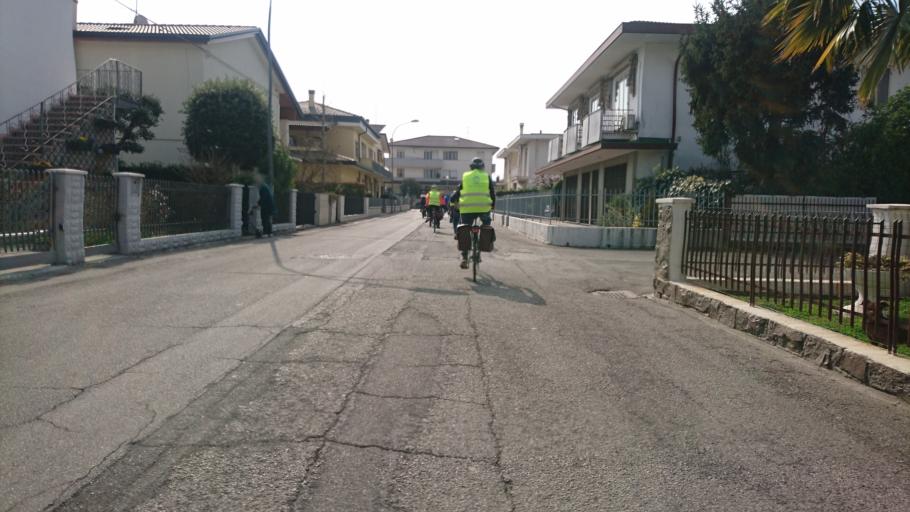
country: IT
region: Veneto
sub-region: Provincia di Padova
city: Abano Terme
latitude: 45.3552
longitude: 11.7658
